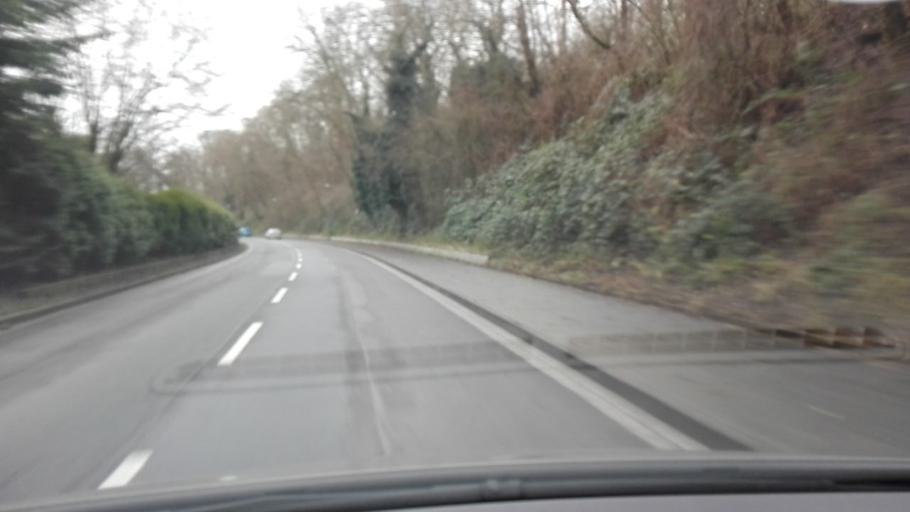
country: DE
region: North Rhine-Westphalia
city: Lanstrop
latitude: 51.5175
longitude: 7.5700
